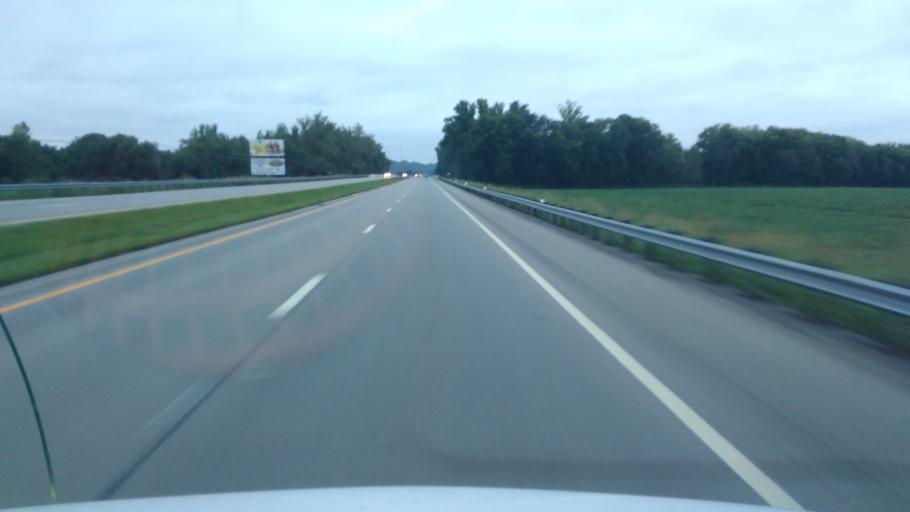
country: US
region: Ohio
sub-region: Pike County
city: Piketon
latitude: 39.0960
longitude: -83.0005
